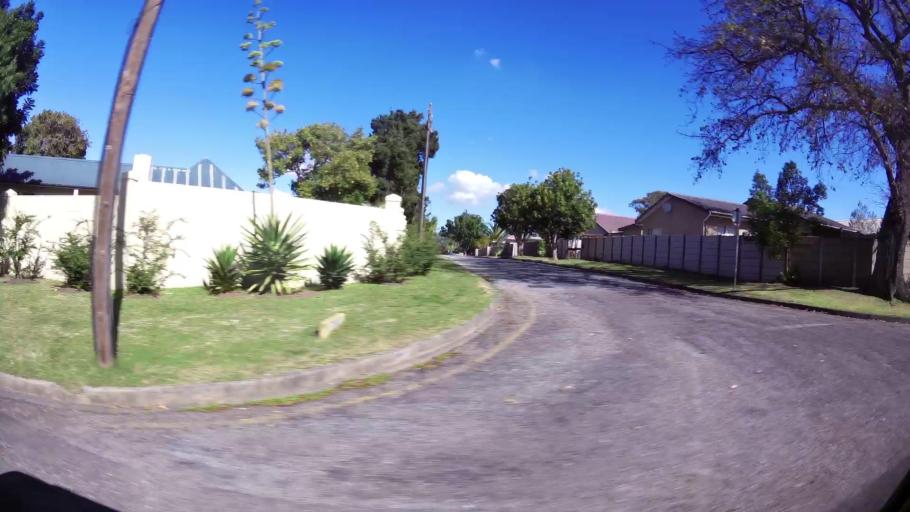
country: ZA
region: Western Cape
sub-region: Eden District Municipality
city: George
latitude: -33.9515
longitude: 22.4783
